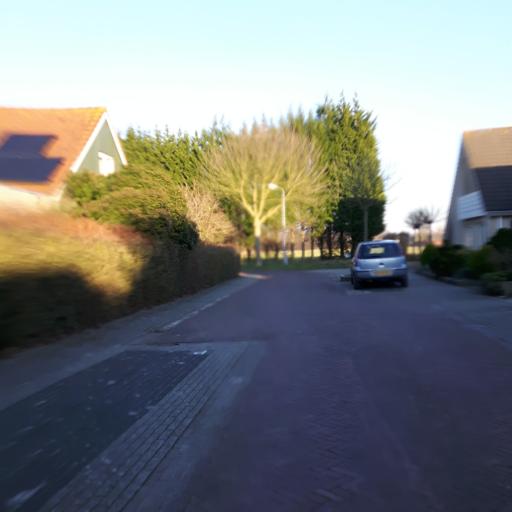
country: NL
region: Zeeland
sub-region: Gemeente Goes
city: Goes
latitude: 51.4912
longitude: 3.9133
